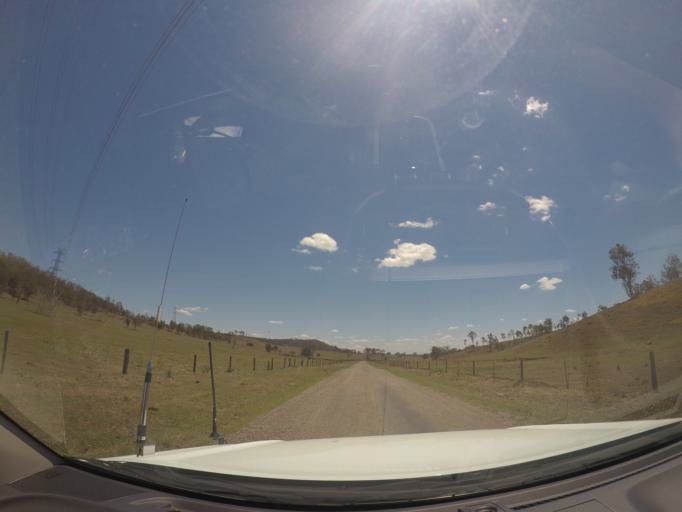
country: AU
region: Queensland
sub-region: Ipswich
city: Redbank Plains
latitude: -27.7499
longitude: 152.8320
